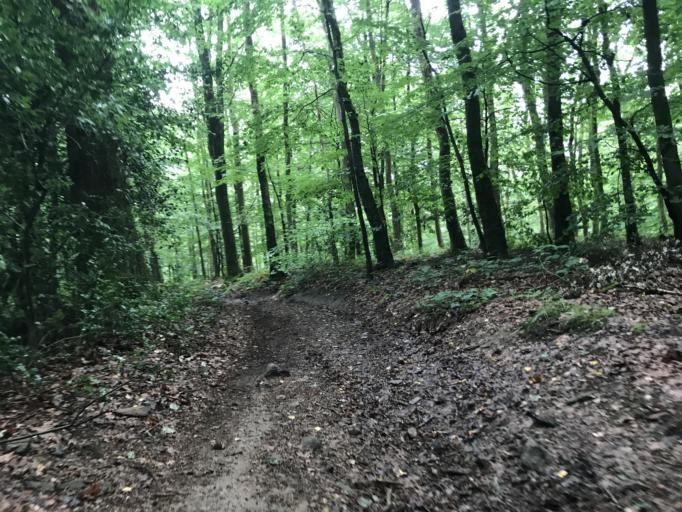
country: FR
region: Champagne-Ardenne
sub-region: Departement des Ardennes
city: Thilay
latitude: 49.8864
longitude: 4.7844
